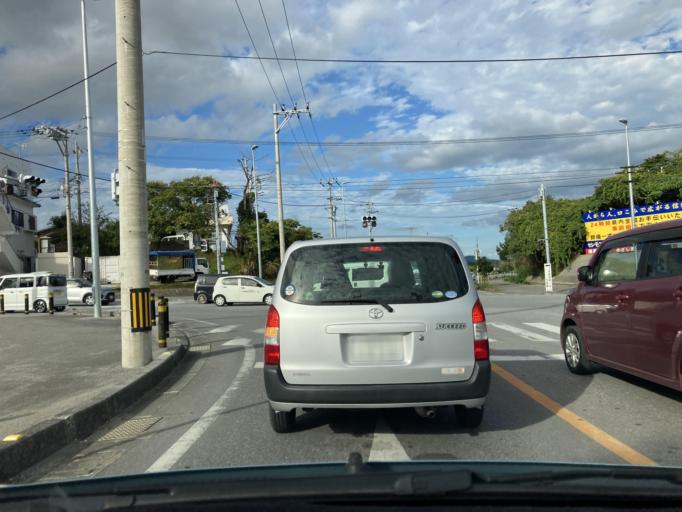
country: JP
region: Okinawa
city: Gushikawa
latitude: 26.3730
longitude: 127.8270
